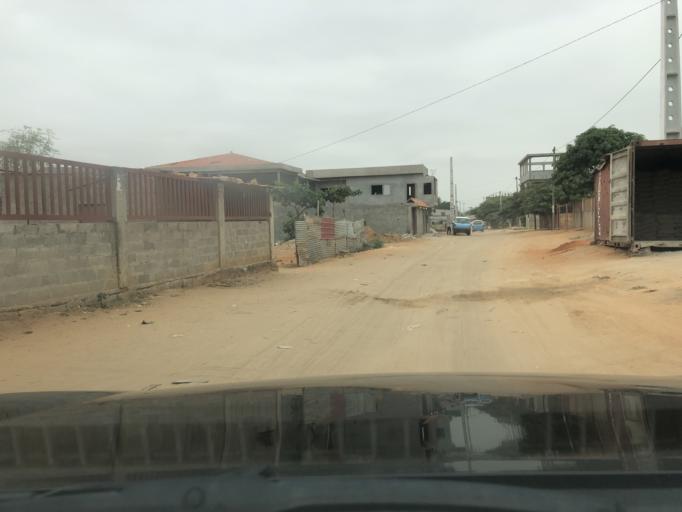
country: AO
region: Luanda
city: Luanda
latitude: -8.9380
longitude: 13.2289
